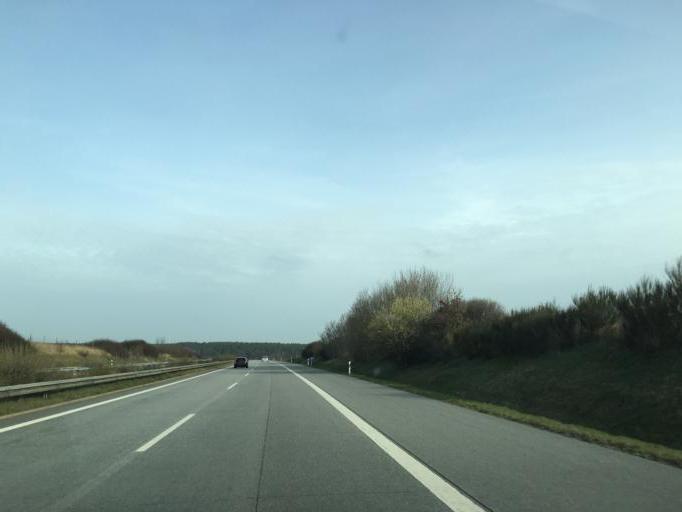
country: DE
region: Mecklenburg-Vorpommern
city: Malchow
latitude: 53.4042
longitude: 12.4447
